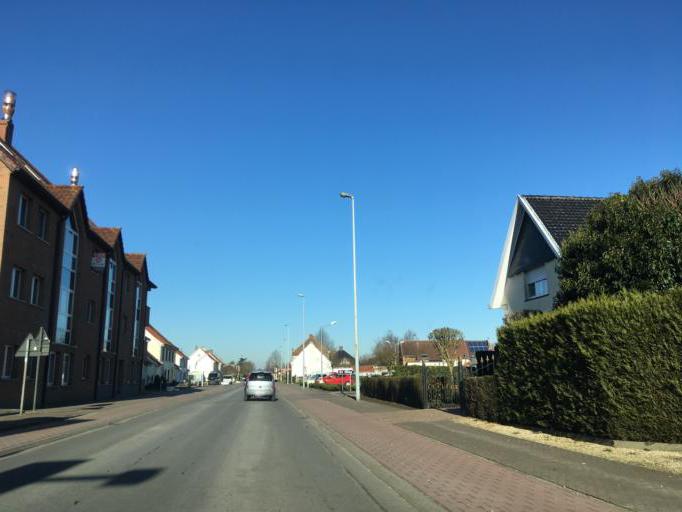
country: BE
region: Flanders
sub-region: Provincie Oost-Vlaanderen
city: Zomergem
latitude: 51.1182
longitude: 3.5714
